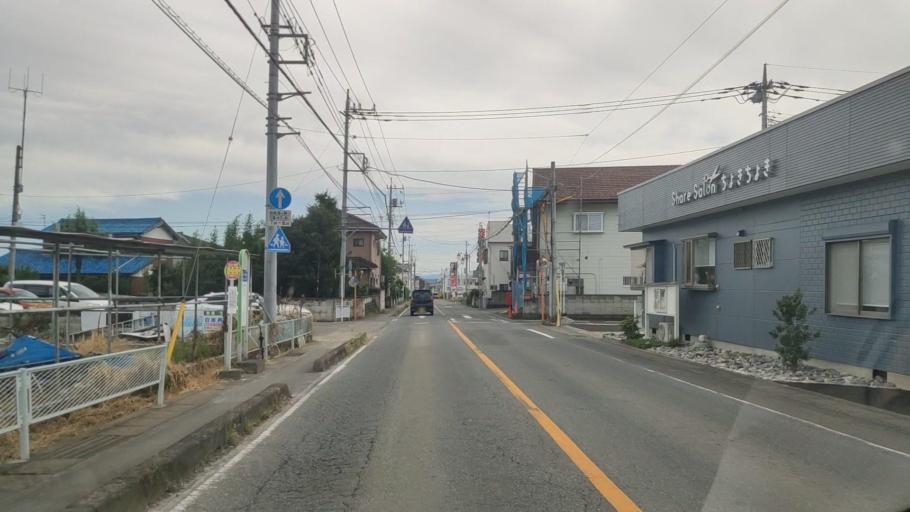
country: JP
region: Gunma
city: Kanekomachi
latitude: 36.3653
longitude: 138.9765
